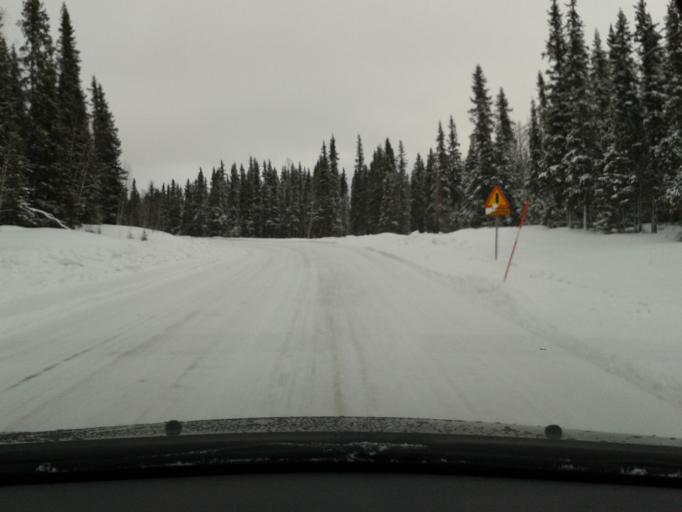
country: SE
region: Vaesterbotten
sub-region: Vilhelmina Kommun
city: Sjoberg
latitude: 65.2275
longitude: 15.9668
